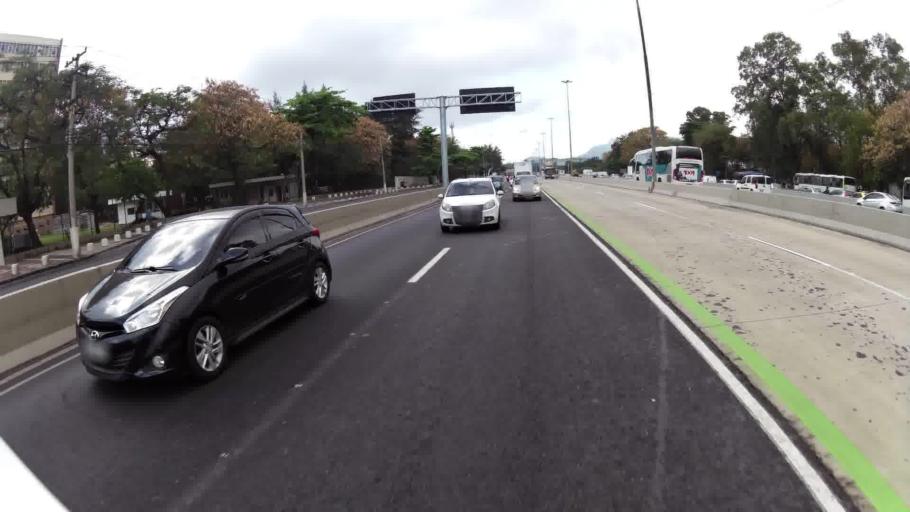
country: BR
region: Rio de Janeiro
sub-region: Rio De Janeiro
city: Rio de Janeiro
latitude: -22.8778
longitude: -43.2411
